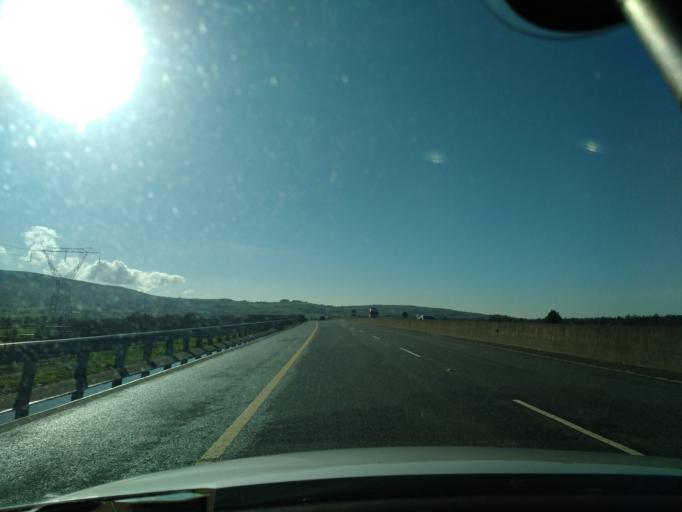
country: IE
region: Munster
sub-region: North Tipperary
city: Nenagh
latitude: 52.8213
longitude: -8.3044
